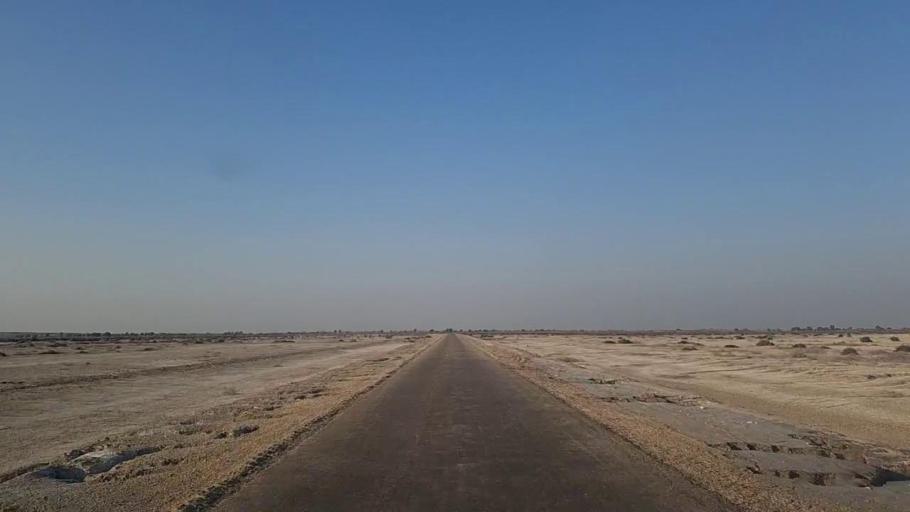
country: PK
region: Sindh
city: Jam Sahib
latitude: 26.3177
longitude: 68.6688
